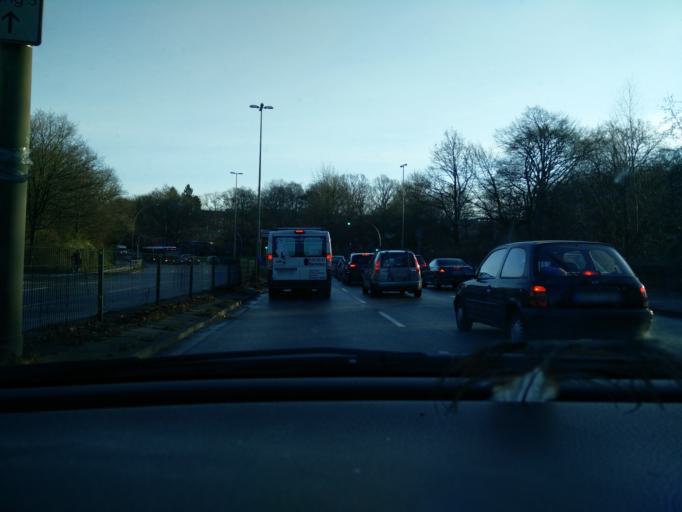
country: DE
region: Hamburg
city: Poppenbuettel
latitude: 53.6562
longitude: 10.0868
